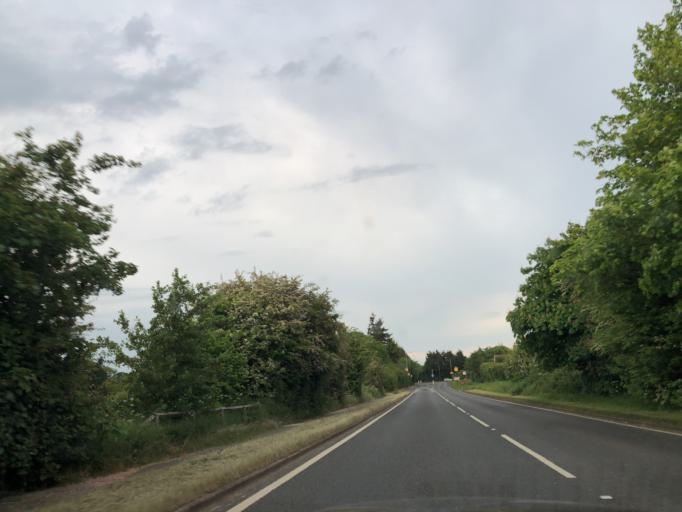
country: GB
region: England
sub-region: Warwickshire
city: Warwick
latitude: 52.2741
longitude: -1.6106
